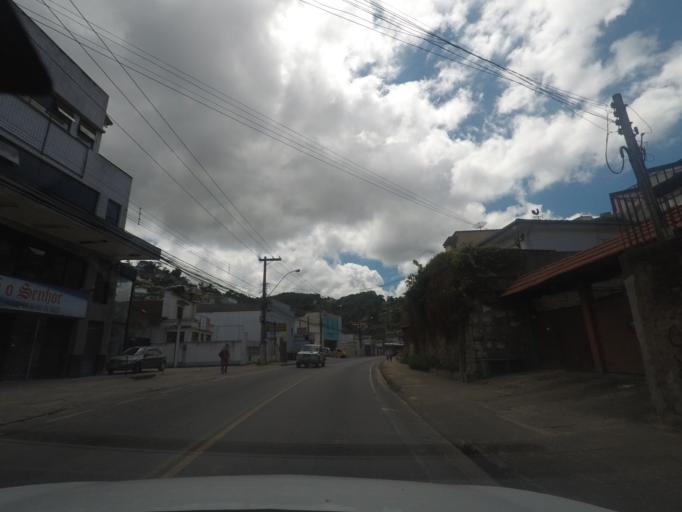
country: BR
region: Rio de Janeiro
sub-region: Teresopolis
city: Teresopolis
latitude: -22.4004
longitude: -42.9750
